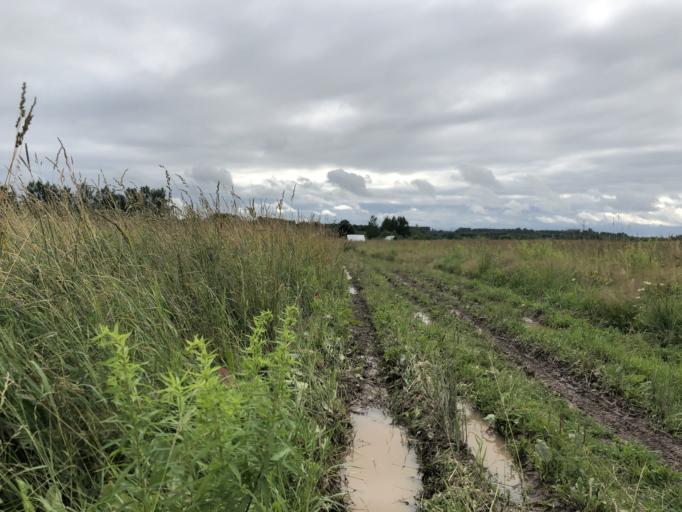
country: RU
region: Tverskaya
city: Rzhev
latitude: 56.2360
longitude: 34.3812
